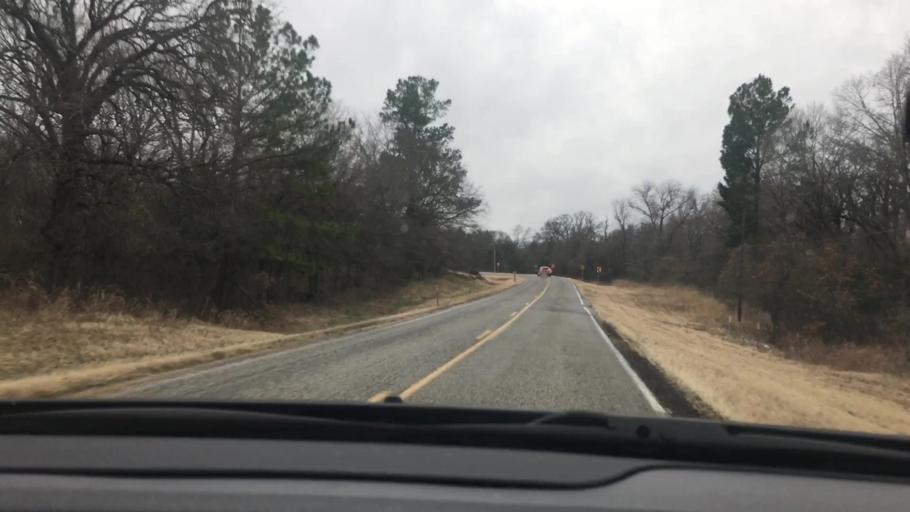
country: US
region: Oklahoma
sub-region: Johnston County
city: Tishomingo
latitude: 34.2113
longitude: -96.6362
